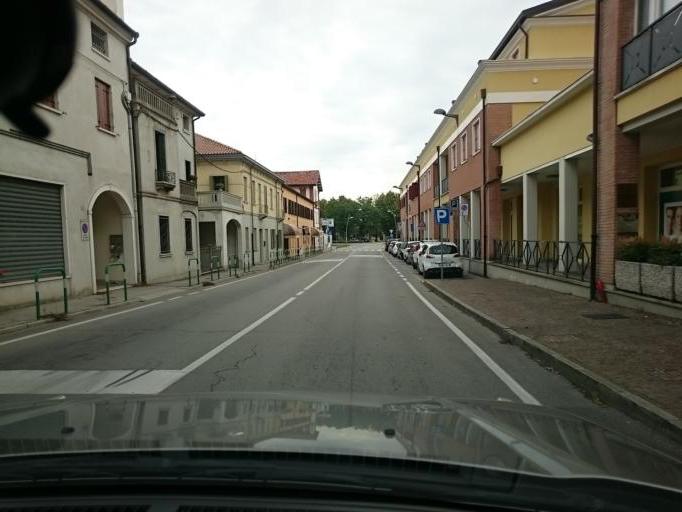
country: IT
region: Veneto
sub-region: Provincia di Padova
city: Piove di Sacco-Piovega
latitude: 45.2982
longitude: 12.0358
